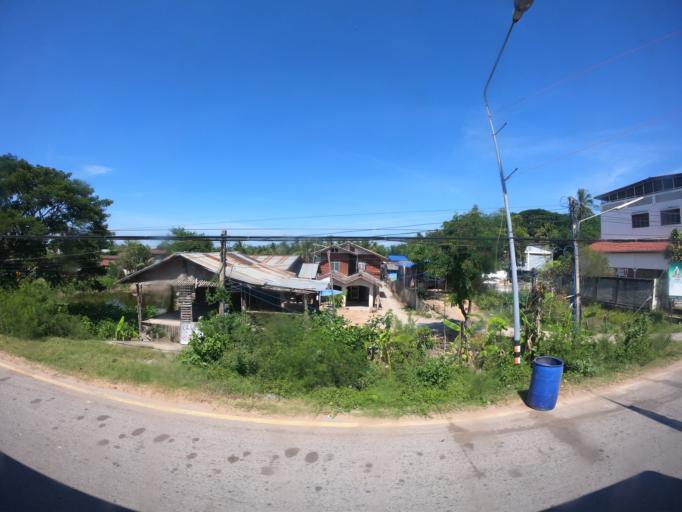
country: TH
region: Khon Kaen
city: Ban Phai
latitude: 16.0570
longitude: 102.7222
